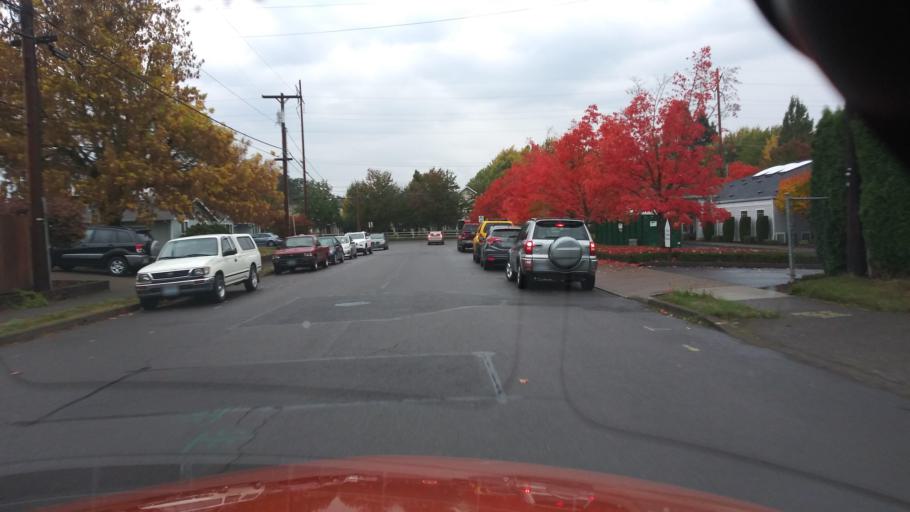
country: US
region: Oregon
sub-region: Washington County
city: Forest Grove
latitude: 45.5224
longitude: -123.0895
